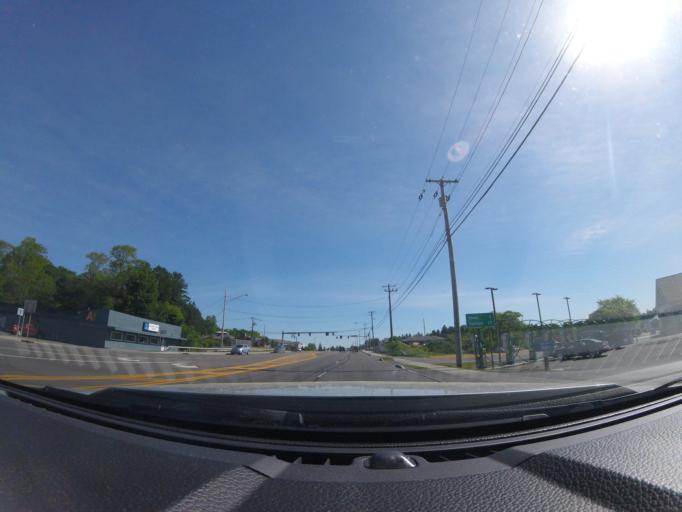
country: US
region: New York
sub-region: Cortland County
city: Munsons Corners
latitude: 42.5985
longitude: -76.2042
